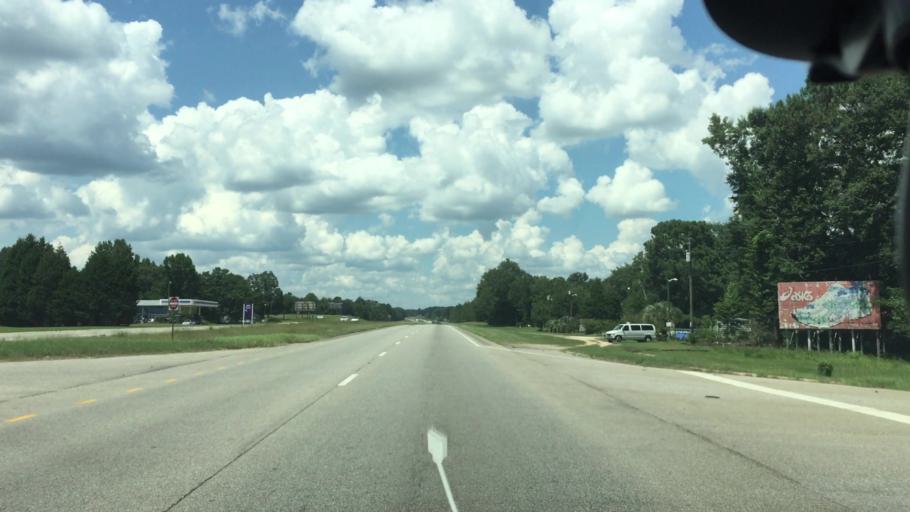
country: US
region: Alabama
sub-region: Pike County
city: Troy
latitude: 31.8541
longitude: -85.9965
